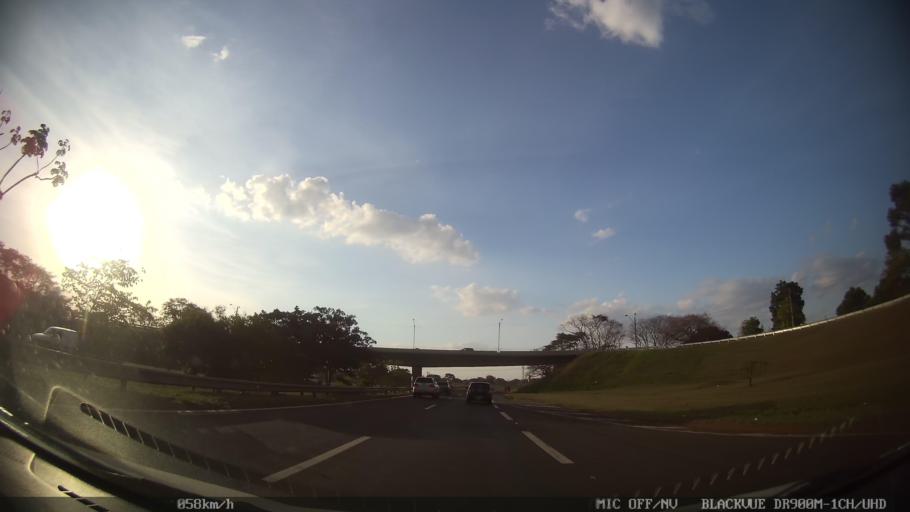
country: BR
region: Sao Paulo
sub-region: Ribeirao Preto
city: Ribeirao Preto
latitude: -21.1227
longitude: -47.7860
